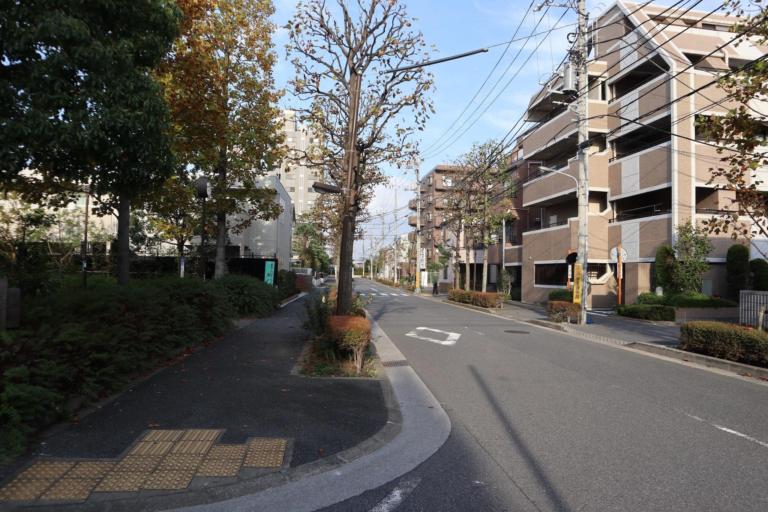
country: JP
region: Tokyo
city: Urayasu
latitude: 35.6844
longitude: 139.8837
